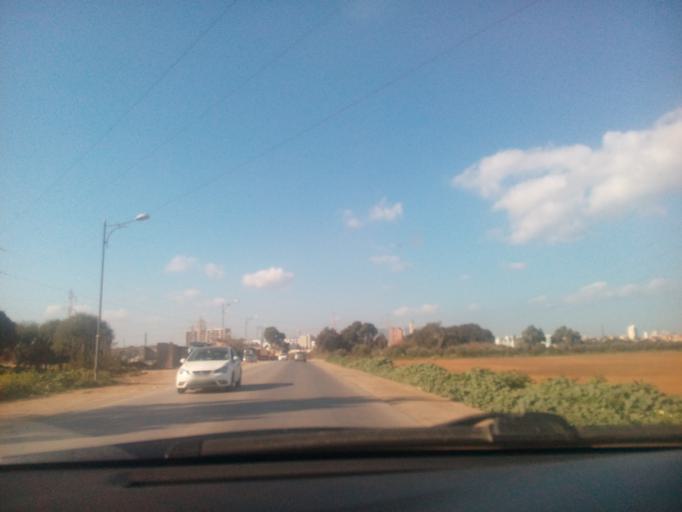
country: DZ
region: Oran
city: Es Senia
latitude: 35.6755
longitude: -0.5929
